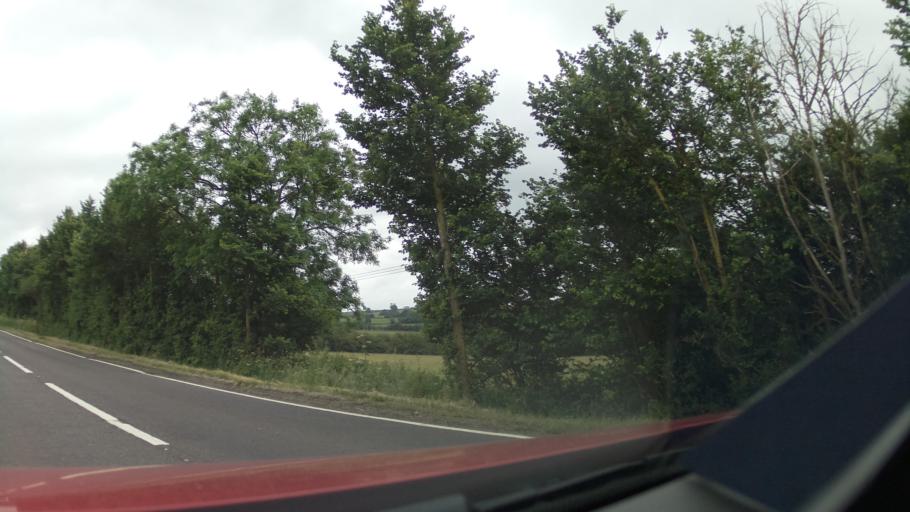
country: GB
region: England
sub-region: Leicestershire
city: Houghton on the Hill
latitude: 52.6246
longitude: -0.9746
